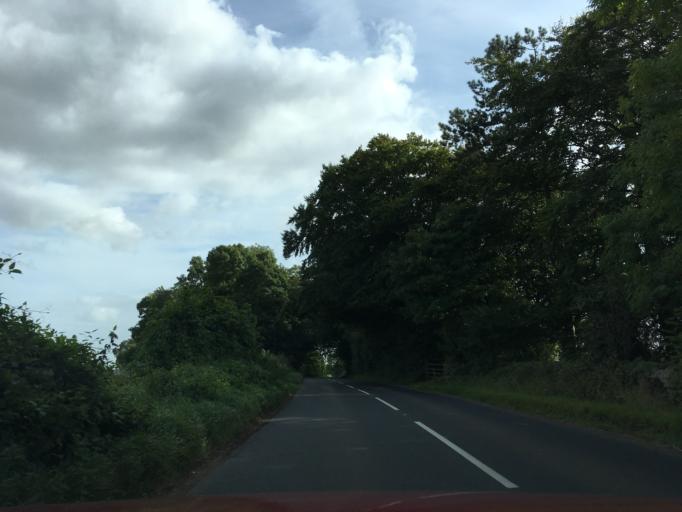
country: GB
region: England
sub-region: Gloucestershire
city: Nailsworth
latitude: 51.6869
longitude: -2.2768
